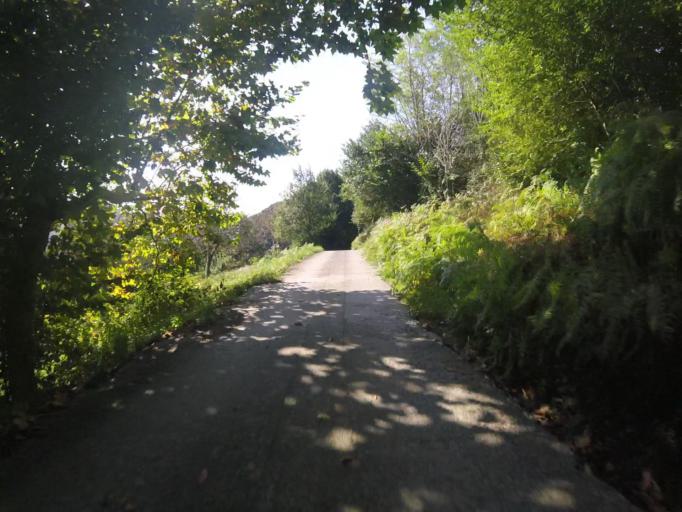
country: ES
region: Basque Country
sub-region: Provincia de Guipuzcoa
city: Irun
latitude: 43.3225
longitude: -1.7443
